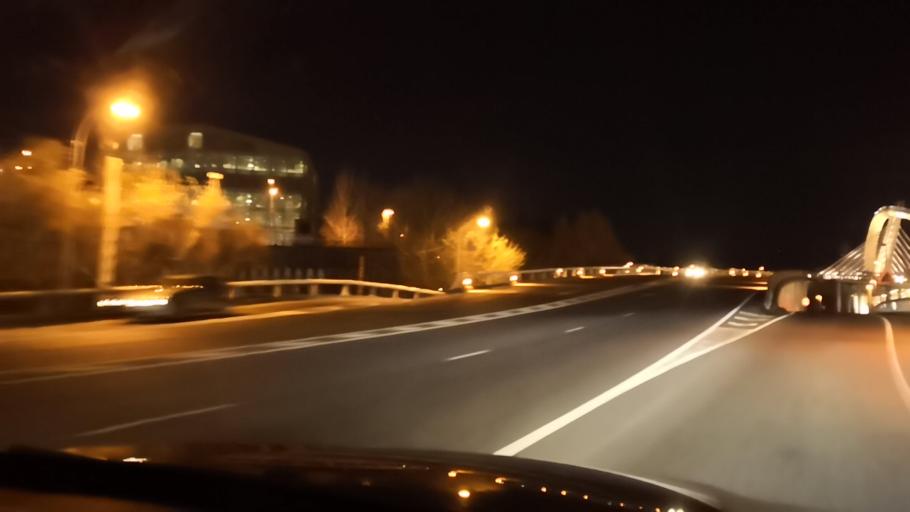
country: ES
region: Galicia
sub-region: Provincia de Ourense
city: Ourense
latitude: 42.3438
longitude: -7.8725
